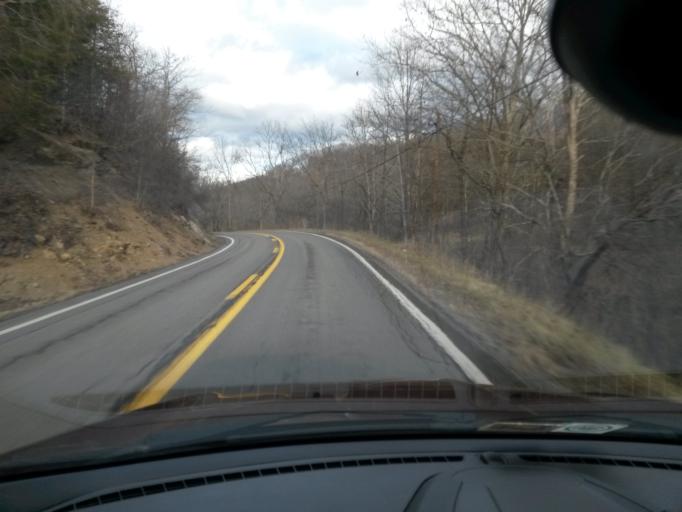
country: US
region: West Virginia
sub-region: Monroe County
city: Union
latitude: 37.4865
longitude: -80.6086
